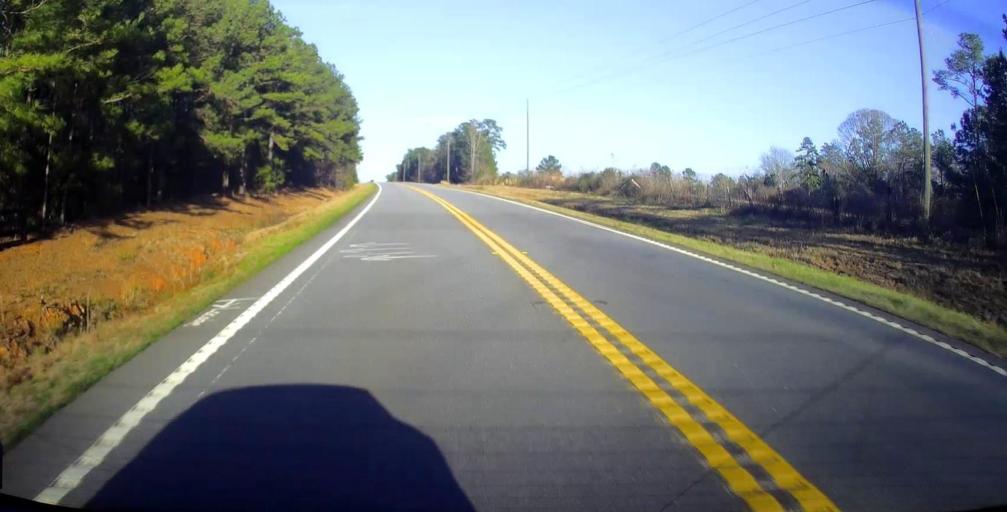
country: US
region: Alabama
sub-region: Chambers County
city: Valley
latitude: 32.7430
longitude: -85.0400
